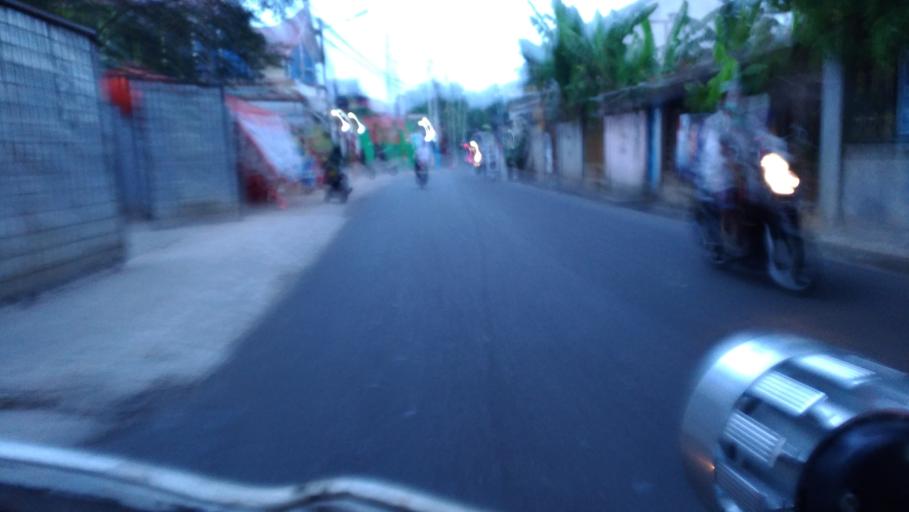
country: ID
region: West Java
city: Depok
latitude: -6.3613
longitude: 106.8846
